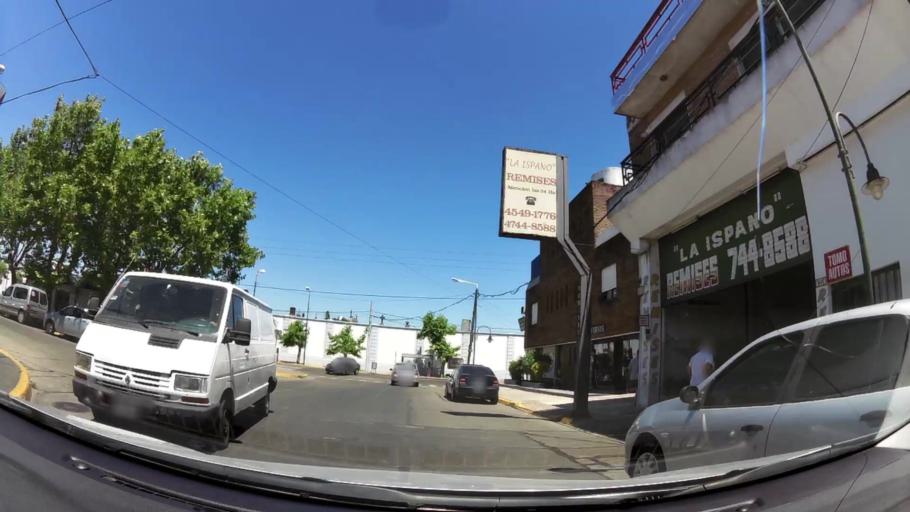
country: AR
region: Buenos Aires
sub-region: Partido de Tigre
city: Tigre
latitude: -34.4557
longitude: -58.5514
